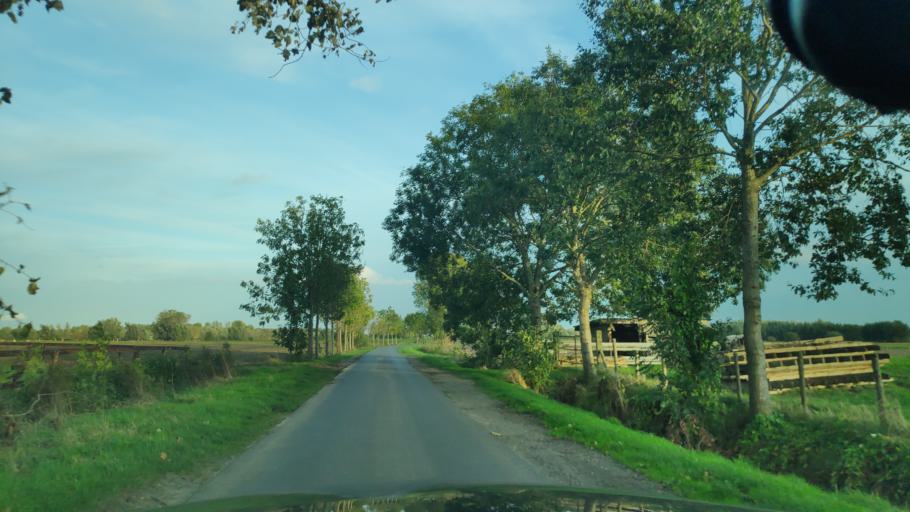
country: BE
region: Flanders
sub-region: Provincie Oost-Vlaanderen
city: Aalter
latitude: 51.1149
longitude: 3.4572
